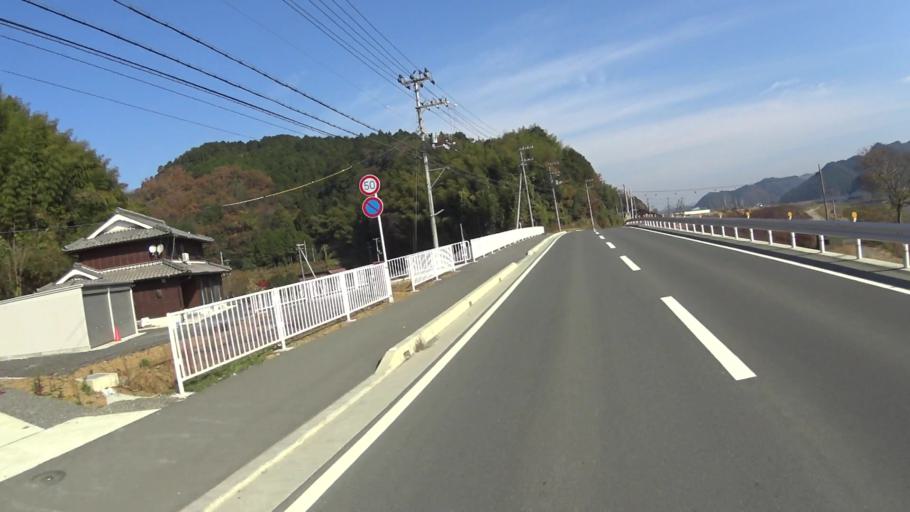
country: JP
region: Kyoto
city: Fukuchiyama
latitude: 35.3684
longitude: 135.1206
